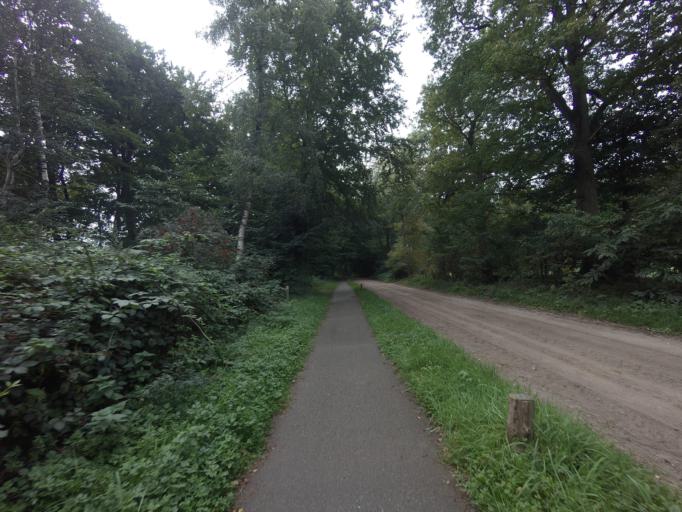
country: DE
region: Lower Saxony
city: Getelo
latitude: 52.4408
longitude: 6.8723
